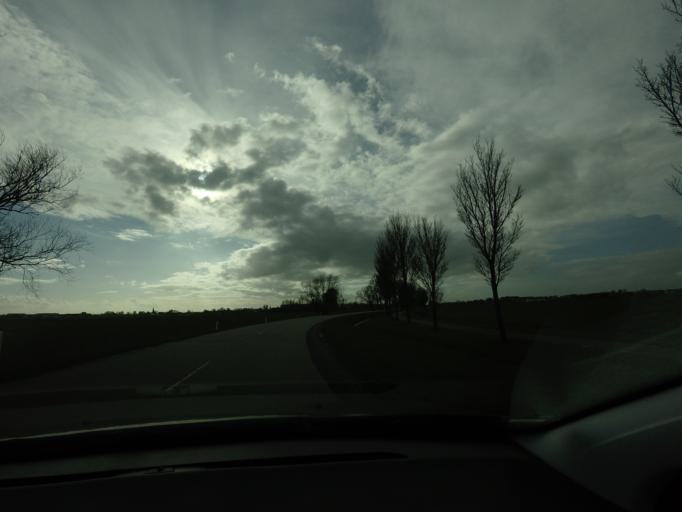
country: NL
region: Friesland
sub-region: Gemeente Boarnsterhim
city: Jirnsum
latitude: 53.0856
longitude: 5.8068
